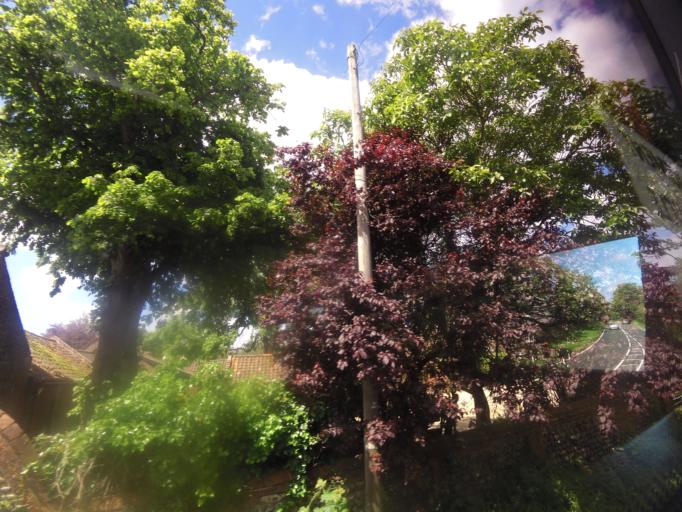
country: GB
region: England
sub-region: Norfolk
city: Cromer
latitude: 52.8979
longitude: 1.3104
